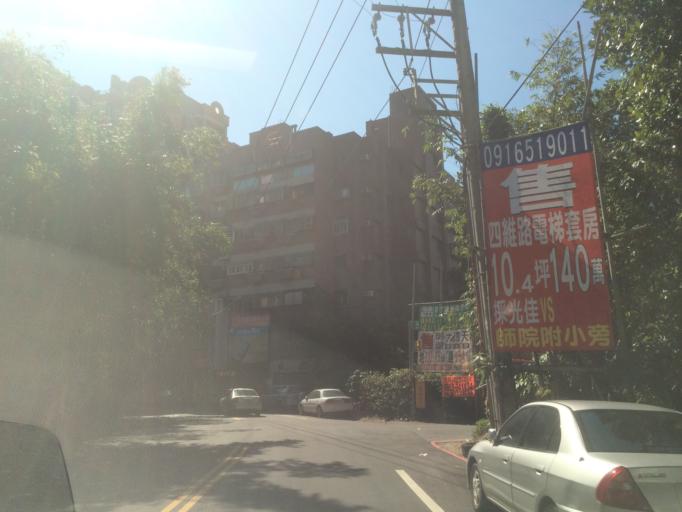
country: TW
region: Taiwan
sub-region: Hsinchu
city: Hsinchu
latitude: 24.7957
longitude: 120.9607
